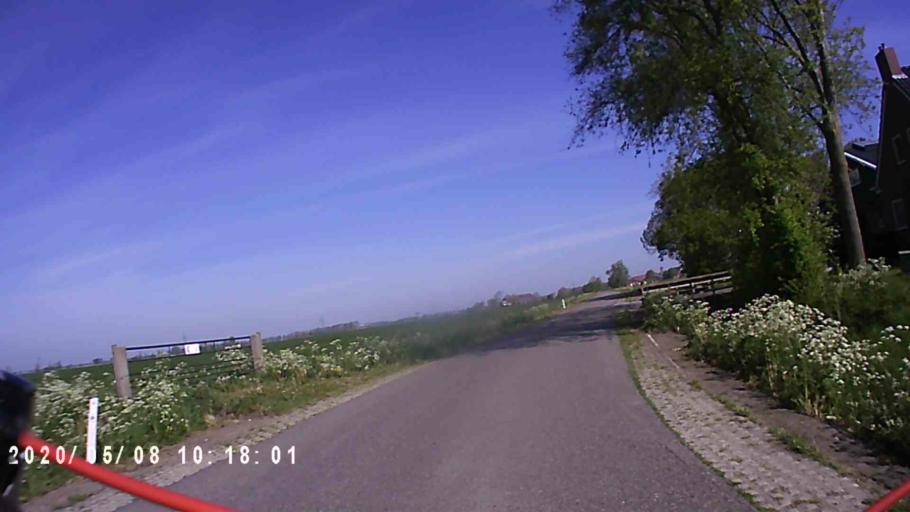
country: NL
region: Groningen
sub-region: Gemeente Winsum
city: Winsum
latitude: 53.2936
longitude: 6.4933
